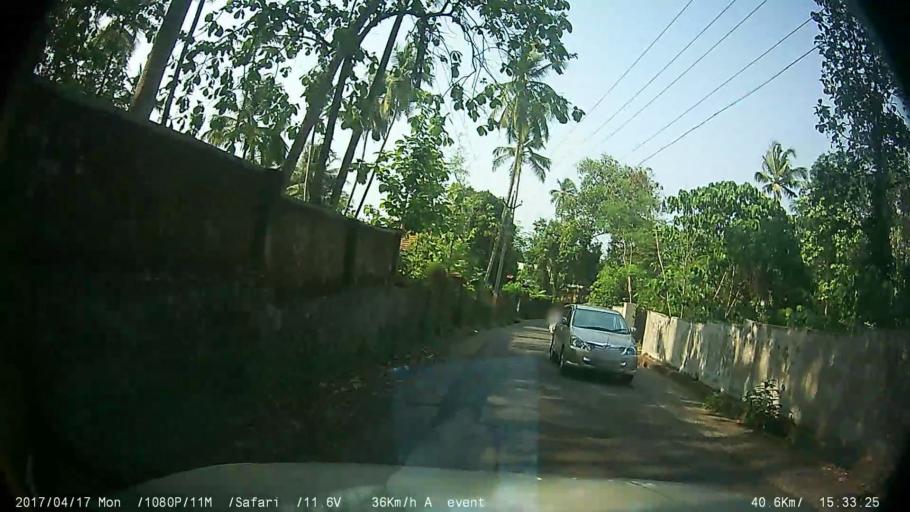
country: IN
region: Kerala
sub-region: Ernakulam
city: Ramamangalam
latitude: 9.9702
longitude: 76.4262
